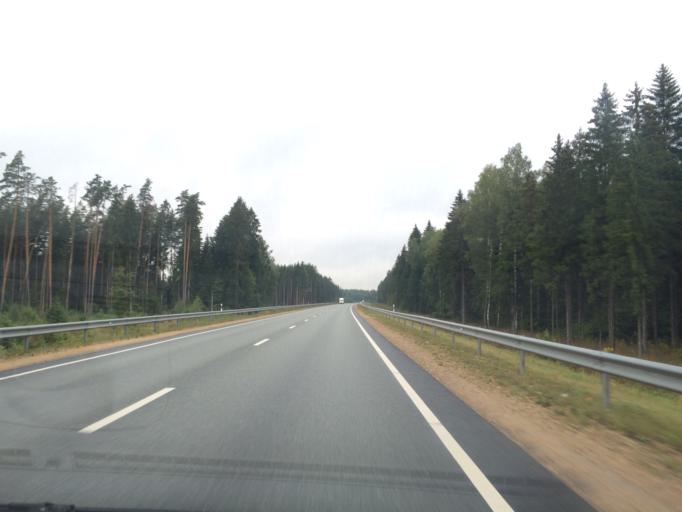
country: LV
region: Ogre
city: Ogre
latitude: 56.8514
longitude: 24.6561
